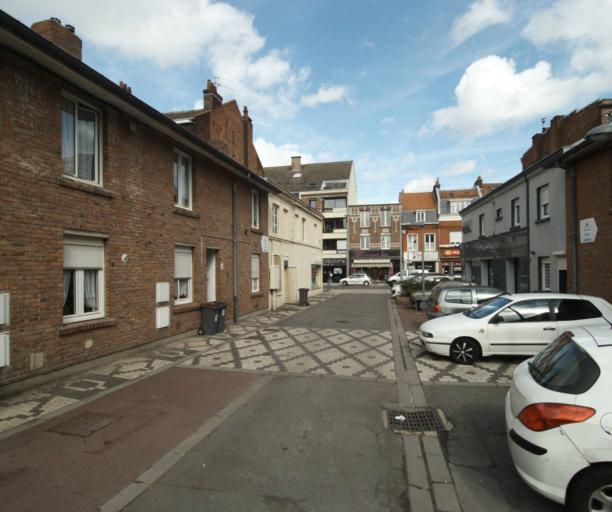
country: FR
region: Nord-Pas-de-Calais
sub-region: Departement du Nord
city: Lambersart
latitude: 50.6396
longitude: 3.0189
